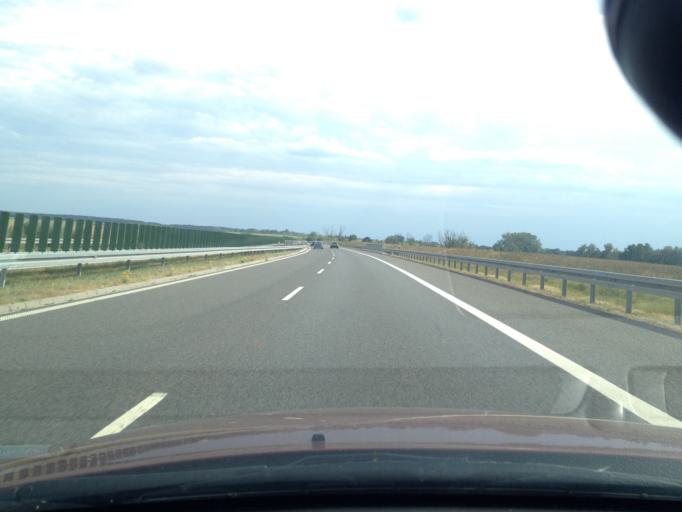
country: PL
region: West Pomeranian Voivodeship
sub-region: Powiat mysliborski
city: Mysliborz
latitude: 52.9912
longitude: 14.8656
